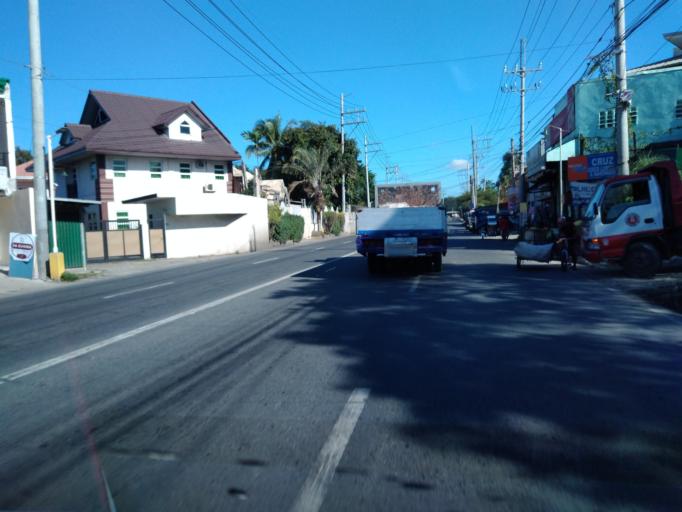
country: PH
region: Central Luzon
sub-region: Province of Bulacan
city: Santa Maria
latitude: 14.8143
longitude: 120.9488
